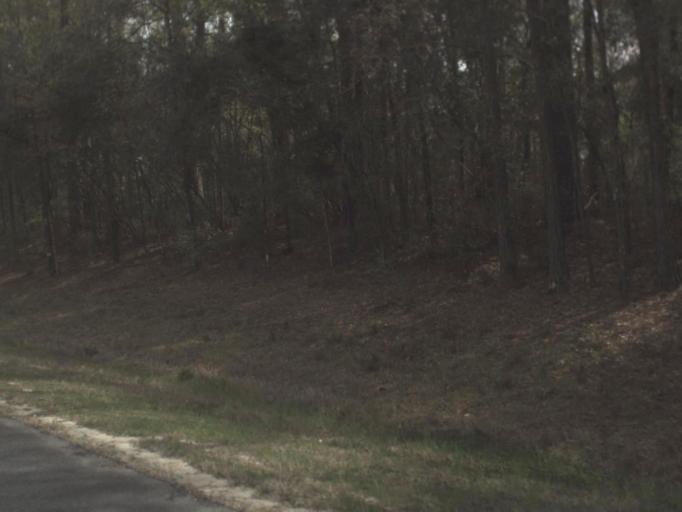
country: US
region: Alabama
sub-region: Geneva County
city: Geneva
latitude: 30.9517
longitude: -85.8695
